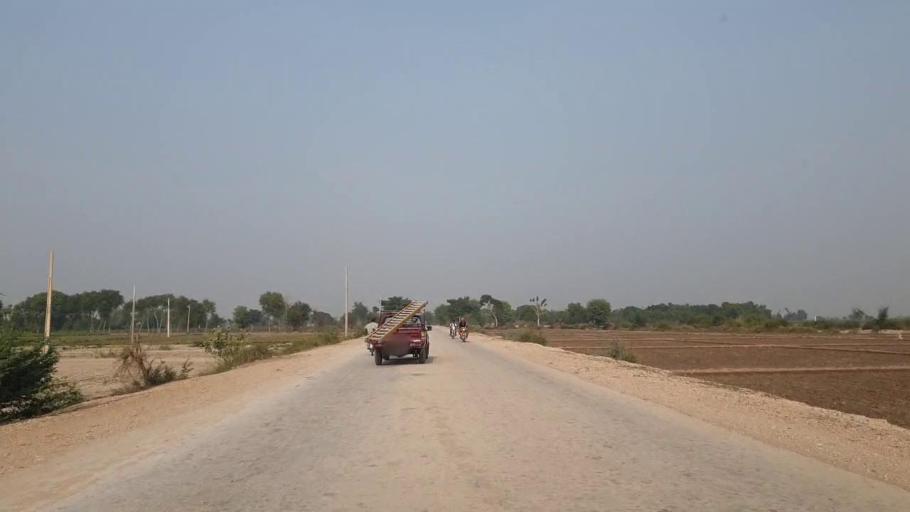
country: PK
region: Sindh
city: Bhan
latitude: 26.5705
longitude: 67.7263
